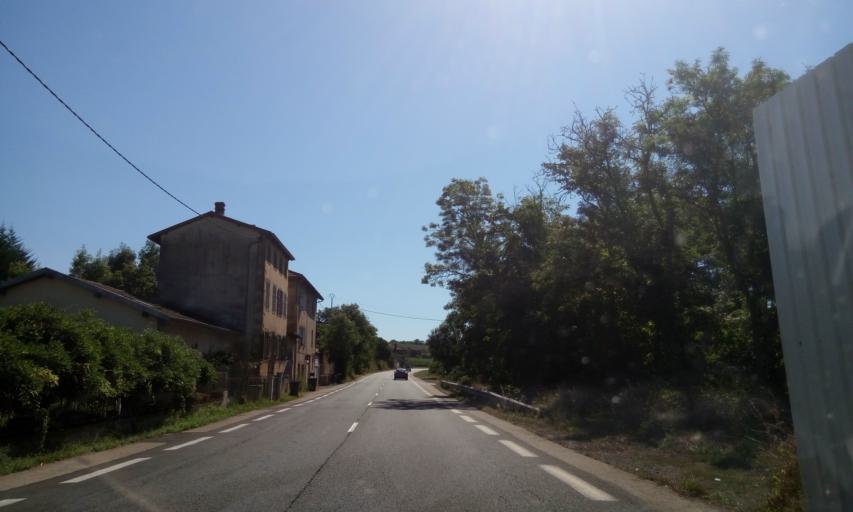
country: FR
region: Rhone-Alpes
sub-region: Departement du Rhone
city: Saint-Verand
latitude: 45.9581
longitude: 4.5205
